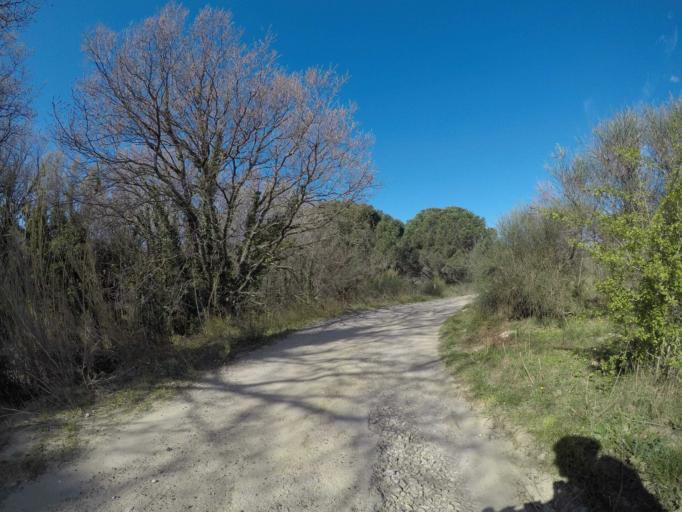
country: FR
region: Languedoc-Roussillon
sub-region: Departement des Pyrenees-Orientales
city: Millas
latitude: 42.7051
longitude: 2.7053
